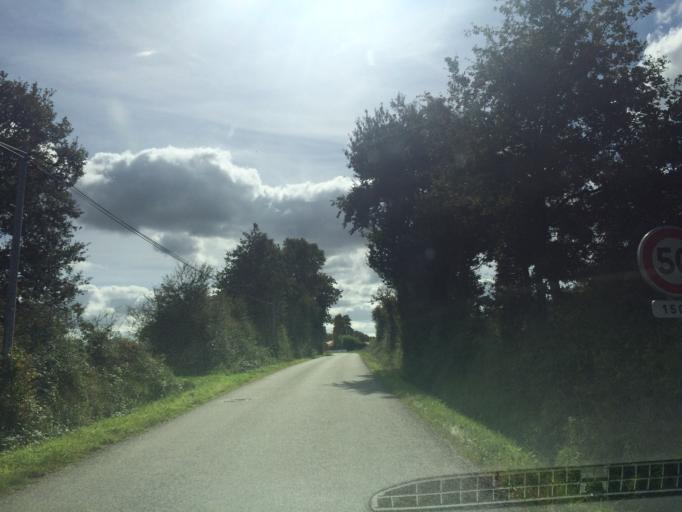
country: FR
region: Pays de la Loire
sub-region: Departement de la Loire-Atlantique
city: Chemere
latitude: 47.1115
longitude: -1.9173
